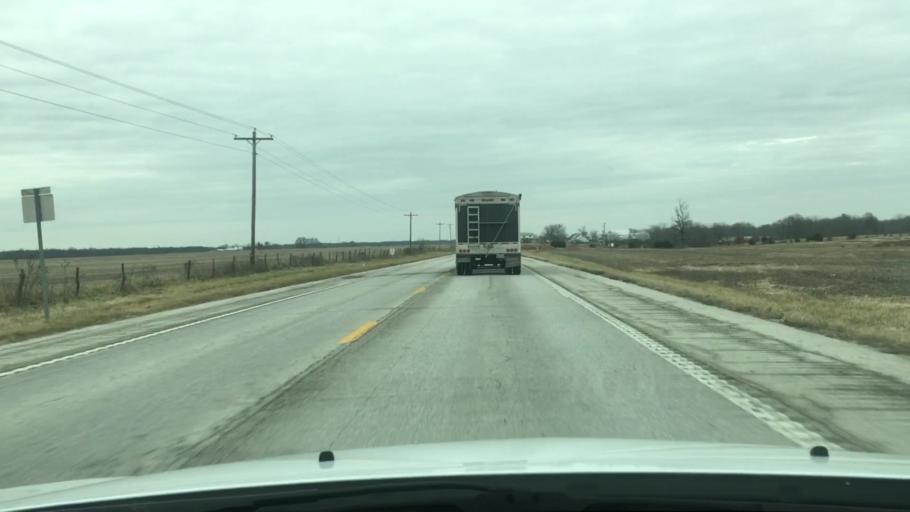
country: US
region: Missouri
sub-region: Montgomery County
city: Wellsville
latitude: 39.1707
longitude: -91.6477
